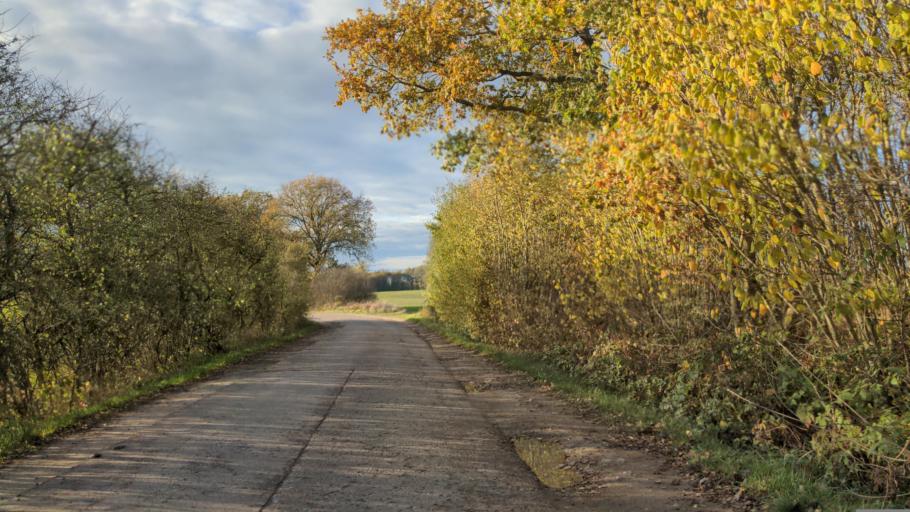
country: DE
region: Schleswig-Holstein
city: Wesenberg
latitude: 53.8420
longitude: 10.5387
